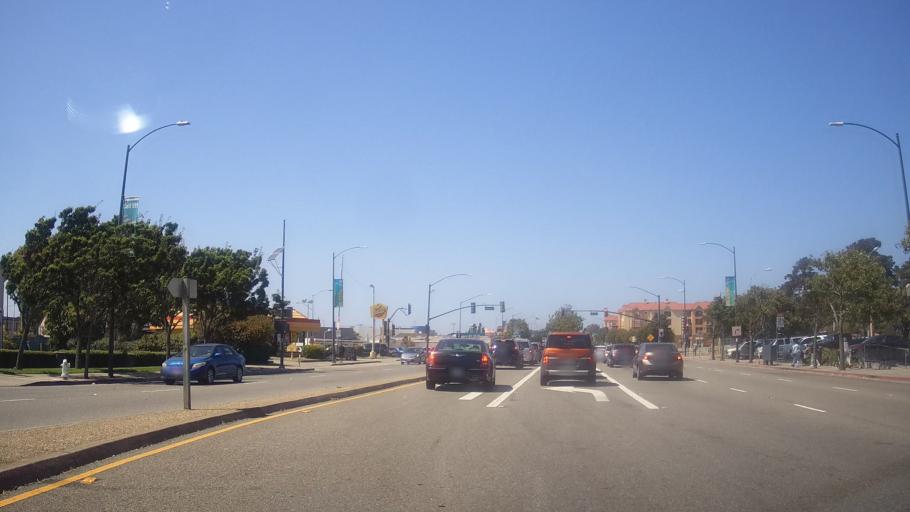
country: US
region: California
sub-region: Contra Costa County
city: El Cerrito
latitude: 37.9245
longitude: -122.3180
